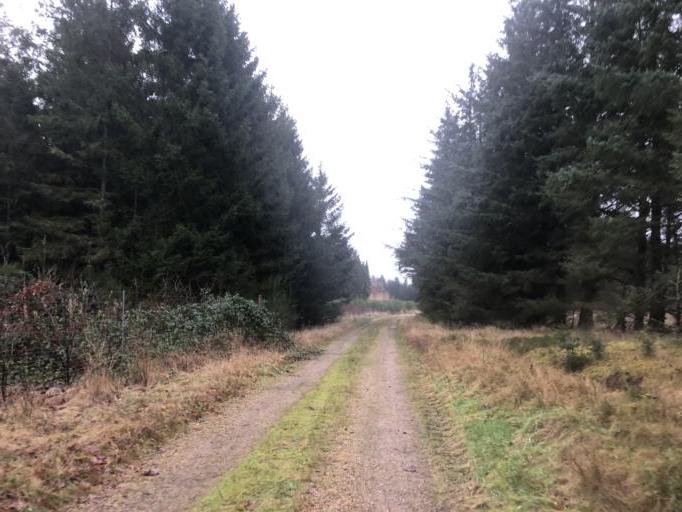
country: DK
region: Central Jutland
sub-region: Holstebro Kommune
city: Ulfborg
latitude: 56.2949
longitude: 8.4397
